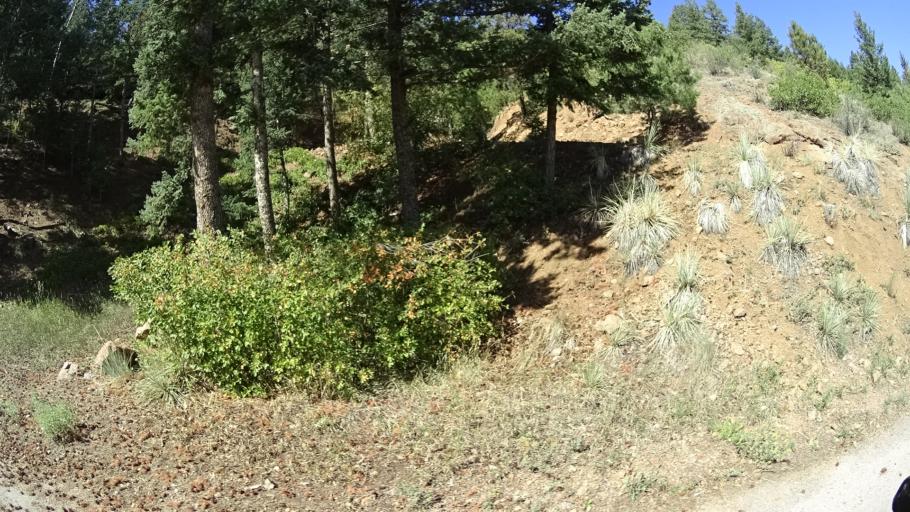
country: US
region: Colorado
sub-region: El Paso County
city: Manitou Springs
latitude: 38.8062
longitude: -104.8812
